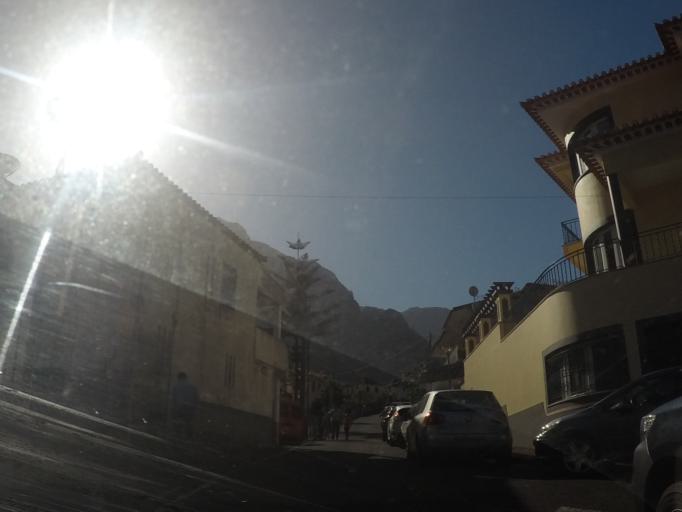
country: PT
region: Madeira
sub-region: Sao Vicente
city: Sao Vicente
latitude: 32.8043
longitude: -16.9650
